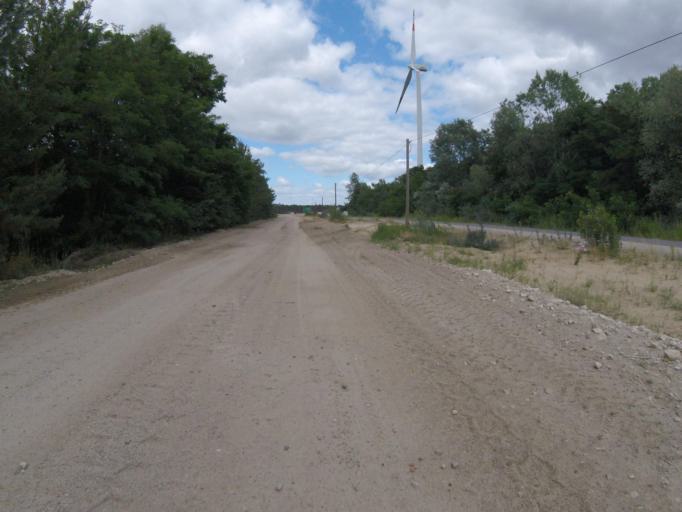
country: DE
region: Brandenburg
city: Wildau
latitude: 52.3242
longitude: 13.6756
